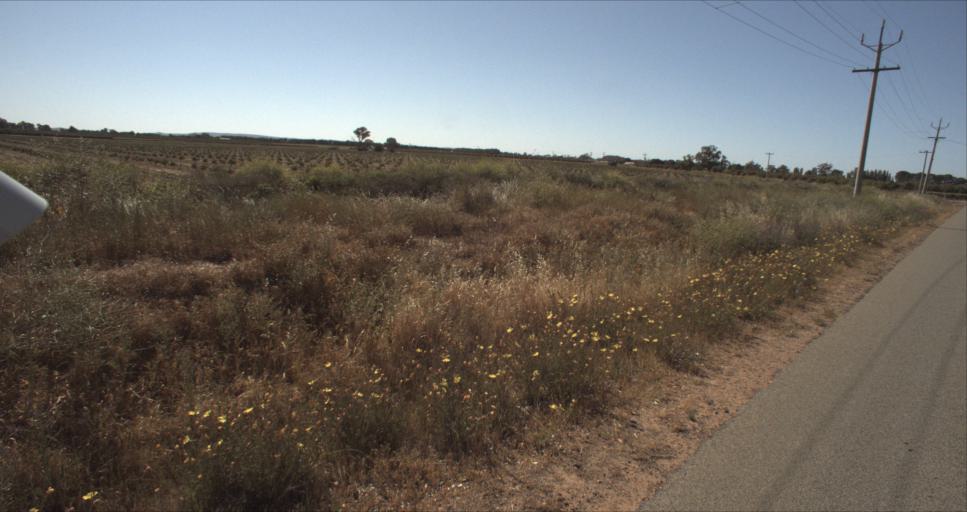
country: AU
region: New South Wales
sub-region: Leeton
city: Leeton
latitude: -34.5381
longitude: 146.3346
